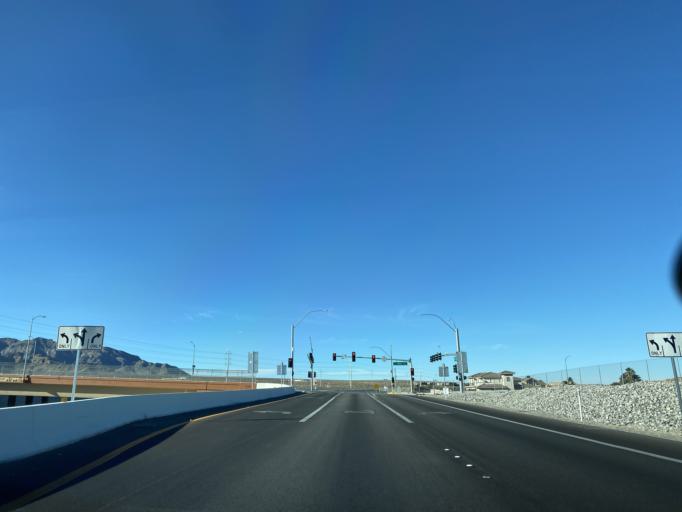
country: US
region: Nevada
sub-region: Clark County
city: Summerlin South
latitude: 36.2612
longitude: -115.3255
